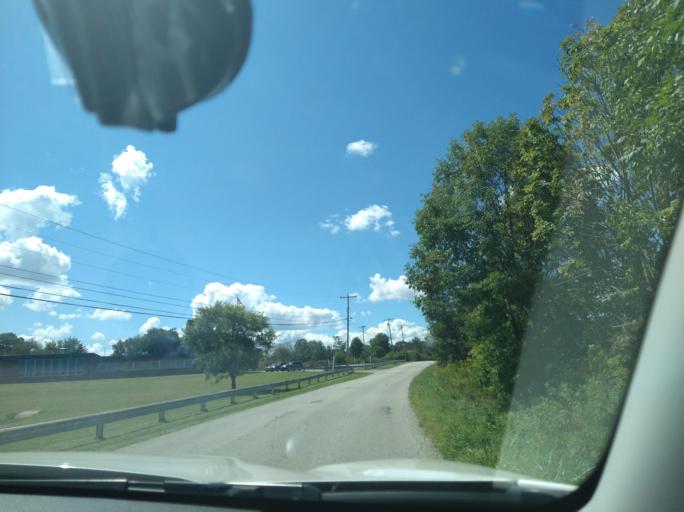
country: US
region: Pennsylvania
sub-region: Fayette County
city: Bear Rocks
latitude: 40.1006
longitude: -79.3573
